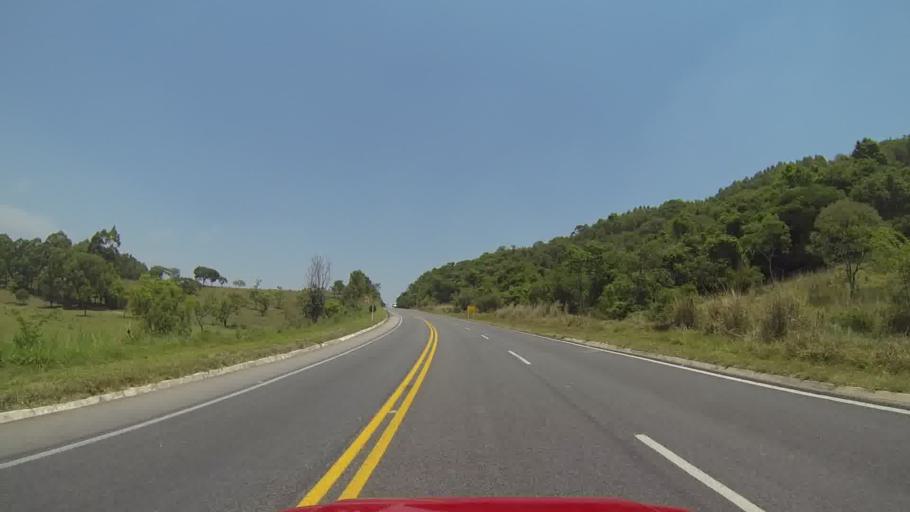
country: BR
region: Minas Gerais
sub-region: Itapecerica
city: Itapecerica
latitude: -20.2891
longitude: -45.1553
